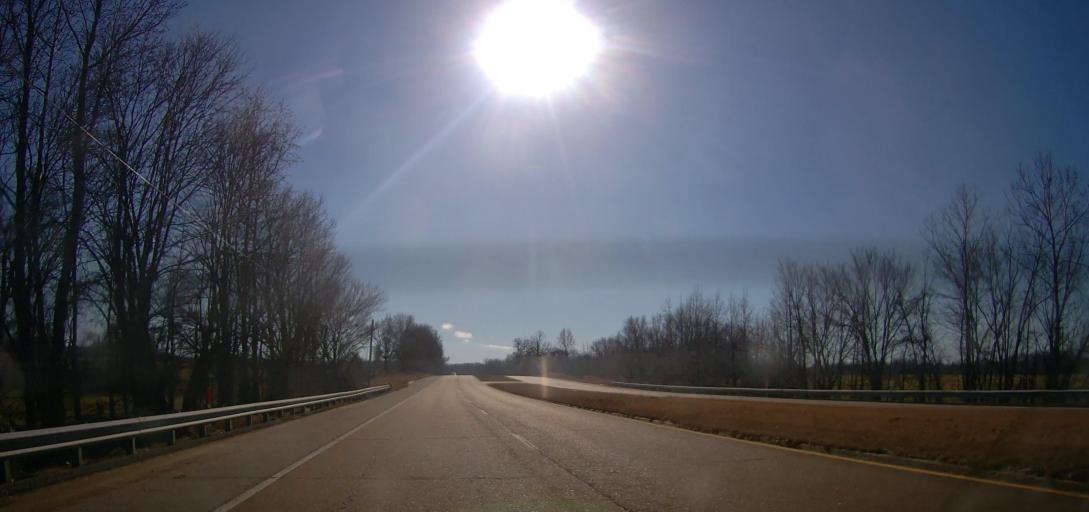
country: US
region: Tennessee
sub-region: Shelby County
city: Bartlett
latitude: 35.2693
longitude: -89.8880
